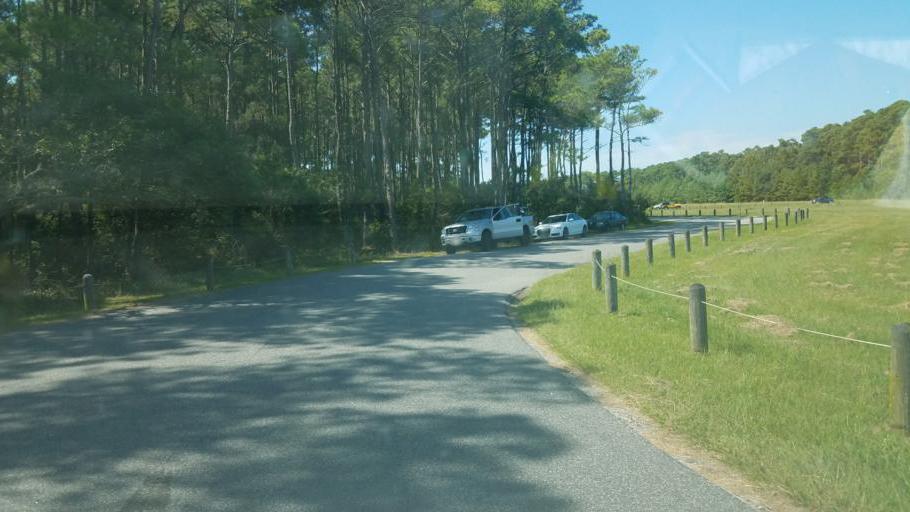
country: US
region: North Carolina
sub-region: Dare County
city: Kill Devil Hills
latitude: 36.0136
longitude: -75.6722
